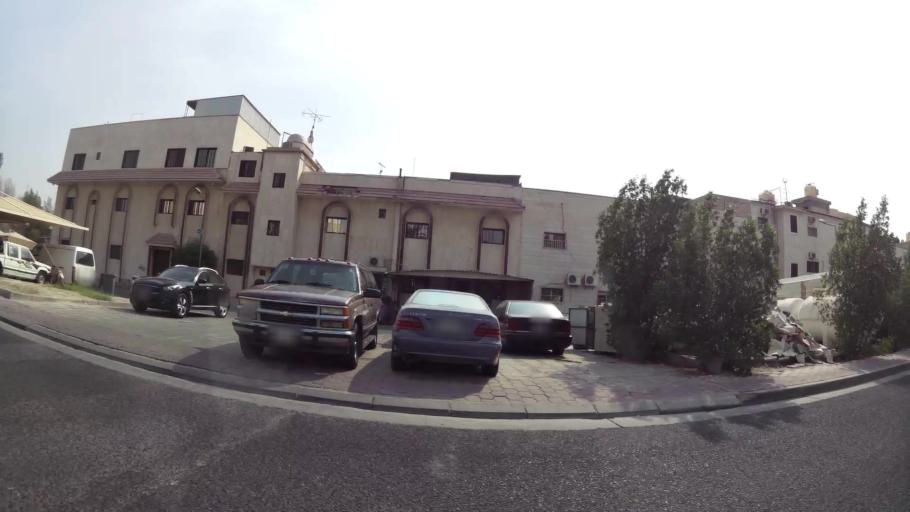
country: KW
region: Al Asimah
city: Ar Rabiyah
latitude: 29.2950
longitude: 47.9320
